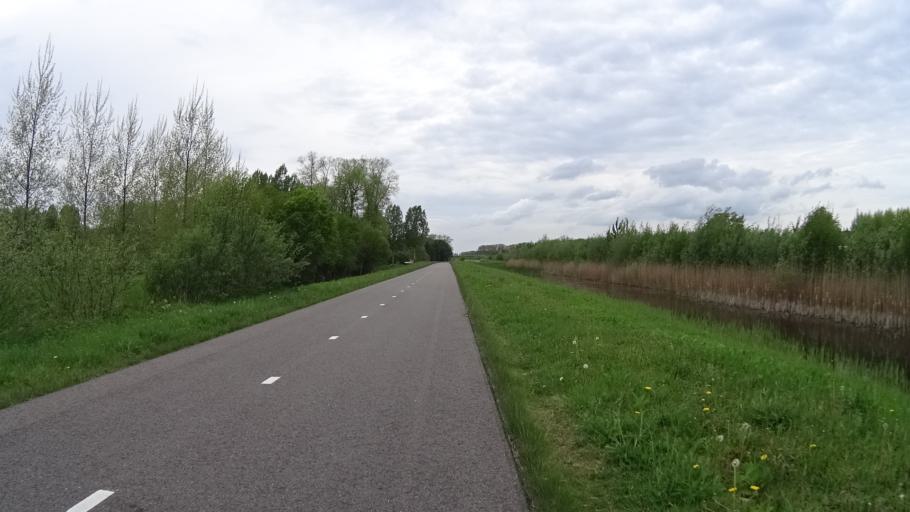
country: NL
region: North Brabant
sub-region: Gemeente Veghel
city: Eerde
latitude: 51.6357
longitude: 5.4798
